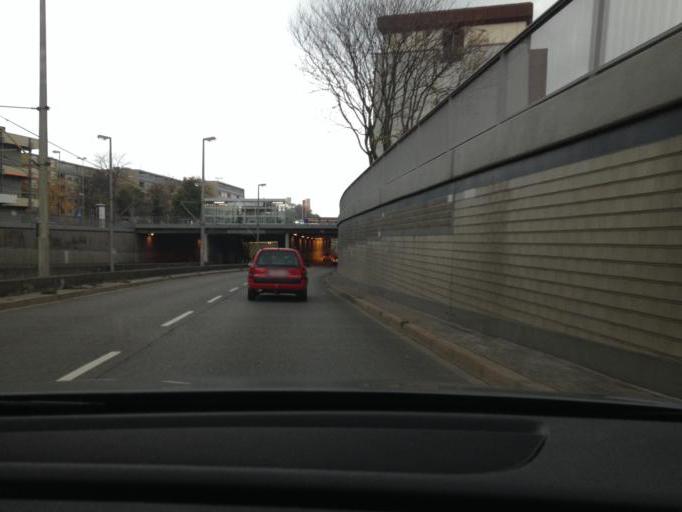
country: DE
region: Rheinland-Pfalz
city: Ludwigshafen am Rhein
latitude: 49.4912
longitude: 8.4384
